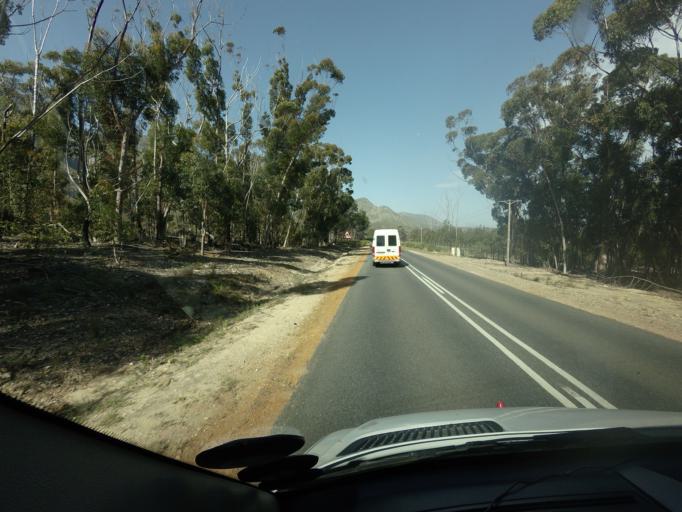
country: ZA
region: Western Cape
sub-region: Overberg District Municipality
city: Hermanus
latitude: -34.4045
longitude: 19.3680
